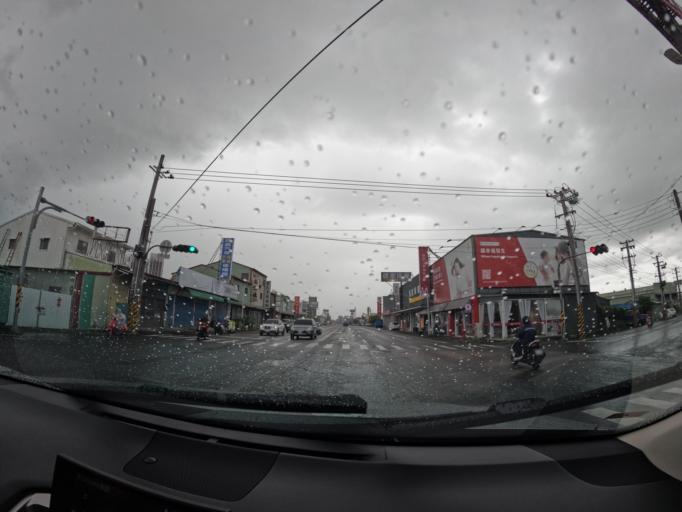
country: TW
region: Taiwan
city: Fengshan
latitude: 22.6507
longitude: 120.3653
